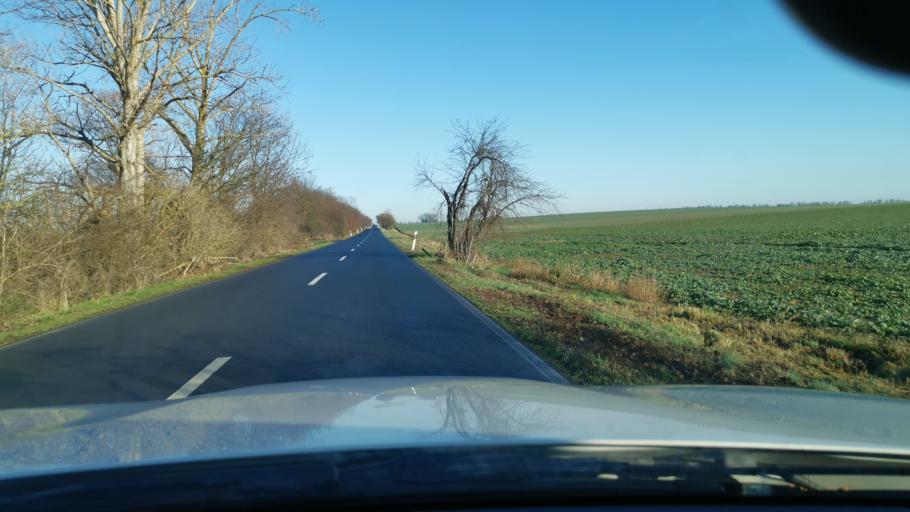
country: DE
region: Saxony-Anhalt
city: Seyda
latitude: 51.9621
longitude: 12.8993
